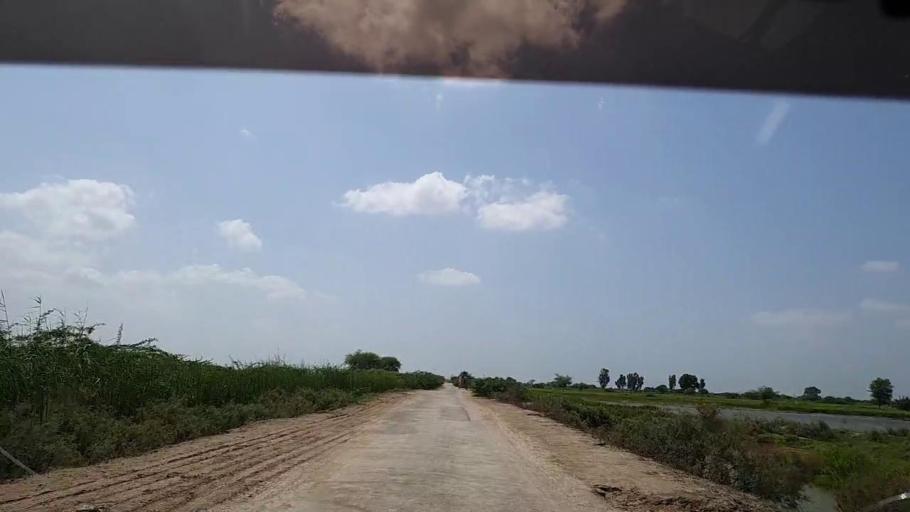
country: PK
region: Sindh
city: Badin
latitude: 24.5631
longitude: 68.7503
